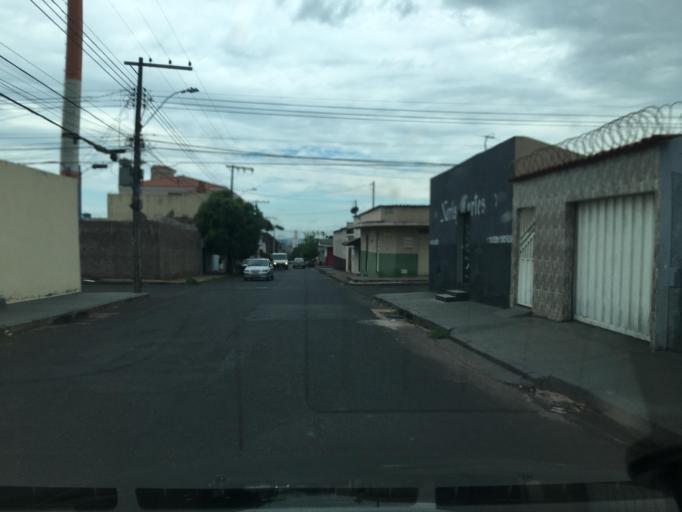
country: BR
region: Minas Gerais
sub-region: Uberlandia
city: Uberlandia
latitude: -18.9325
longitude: -48.3138
